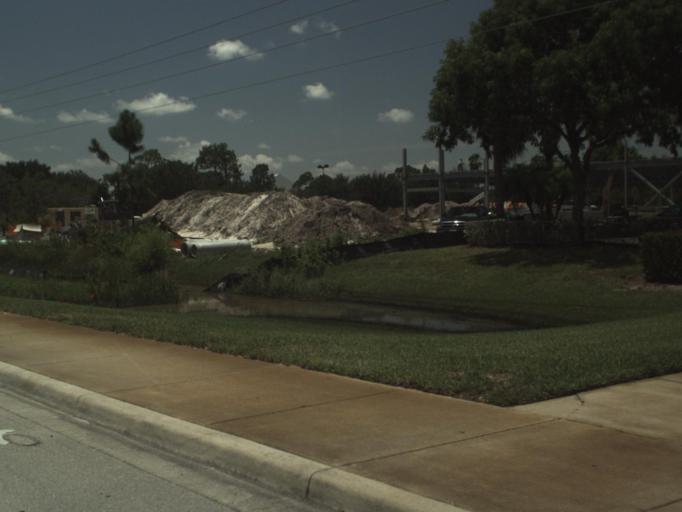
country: US
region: Florida
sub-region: Martin County
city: North River Shores
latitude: 27.2583
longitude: -80.2809
